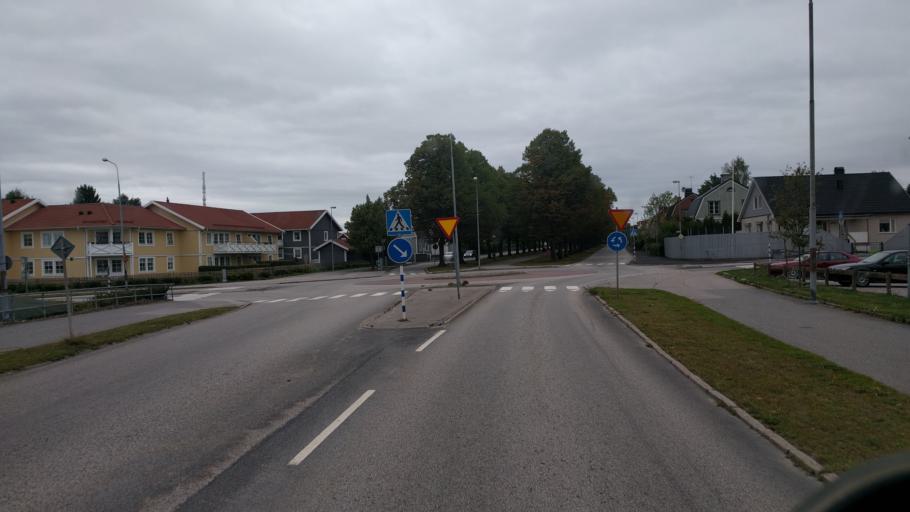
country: SE
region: Kalmar
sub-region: Vasterviks Kommun
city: Vaestervik
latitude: 57.7542
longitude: 16.6244
